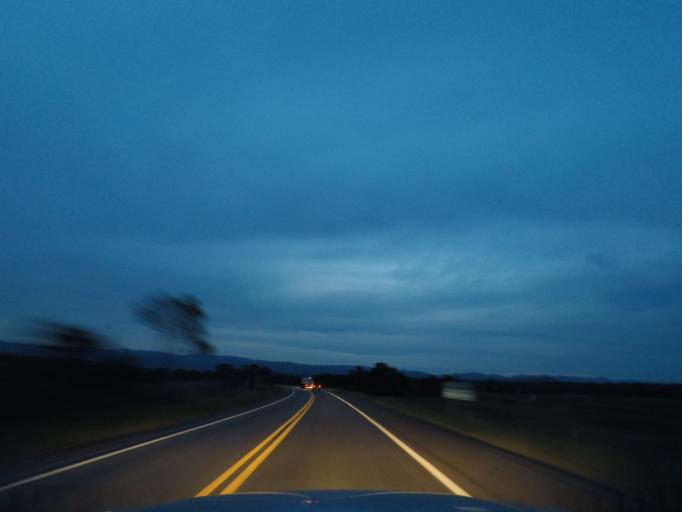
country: BR
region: Bahia
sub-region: Andarai
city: Vera Cruz
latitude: -12.4948
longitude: -41.3031
